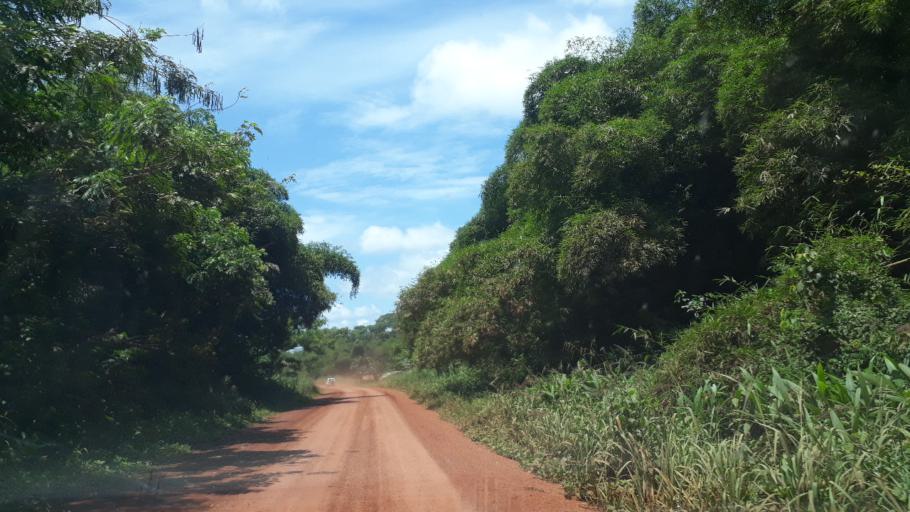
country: CD
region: Eastern Province
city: Kisangani
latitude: 0.5480
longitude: 25.8859
